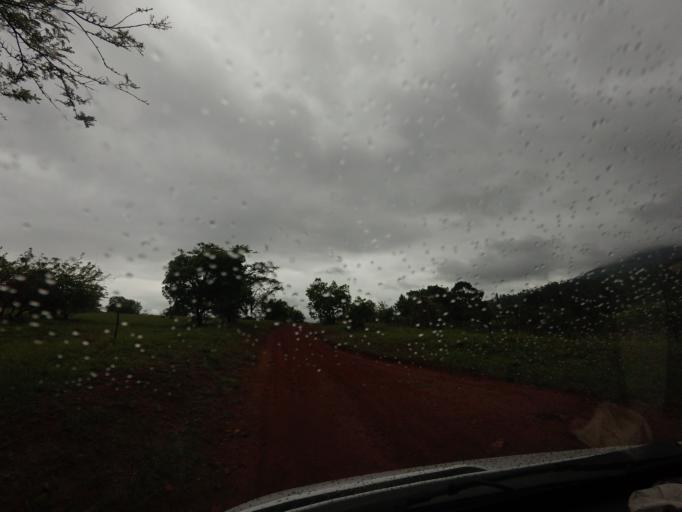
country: SZ
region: Hhohho
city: Lobamba
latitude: -26.4670
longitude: 31.1762
